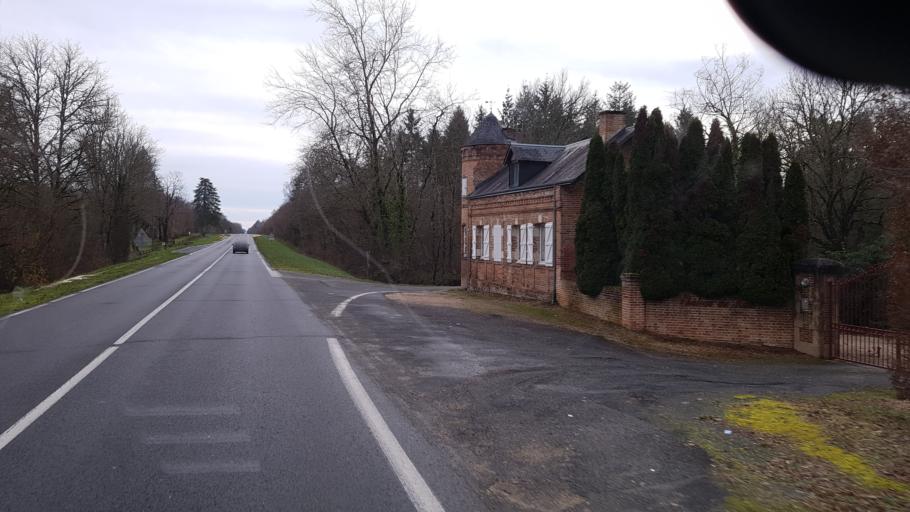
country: FR
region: Centre
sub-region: Departement du Loiret
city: La Ferte-Saint-Aubin
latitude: 47.6880
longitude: 1.9588
